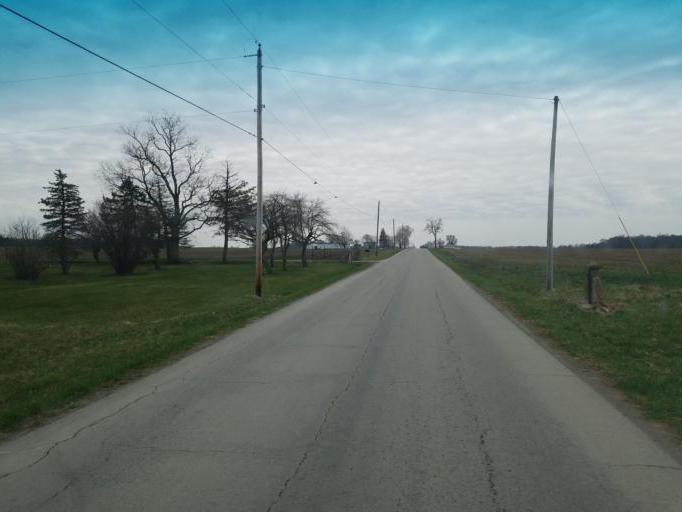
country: US
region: Ohio
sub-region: Wyandot County
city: Upper Sandusky
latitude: 40.8644
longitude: -83.2226
